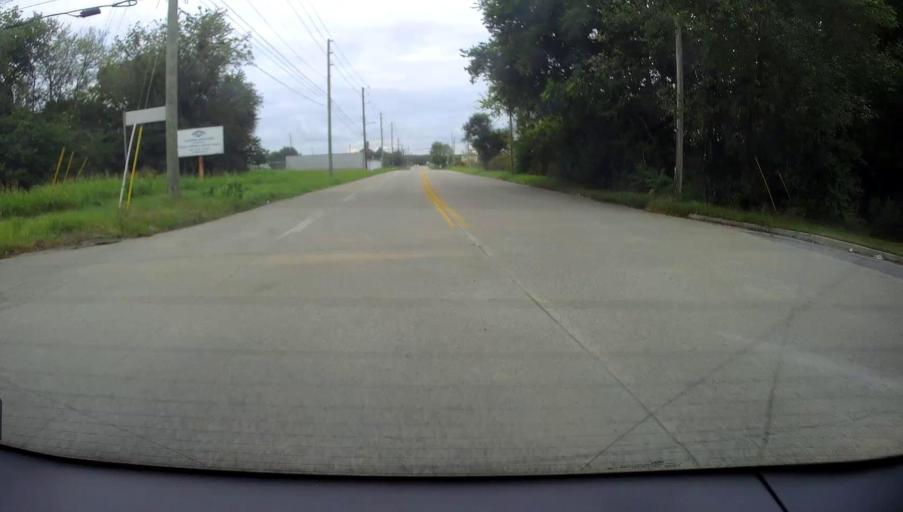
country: US
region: Georgia
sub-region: Bibb County
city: Macon
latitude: 32.8190
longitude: -83.6318
